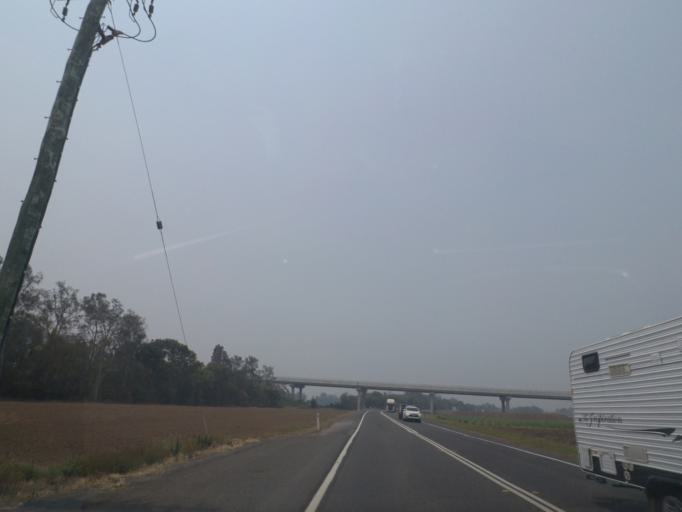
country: AU
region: New South Wales
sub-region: Richmond Valley
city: Evans Head
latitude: -29.0005
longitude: 153.4392
